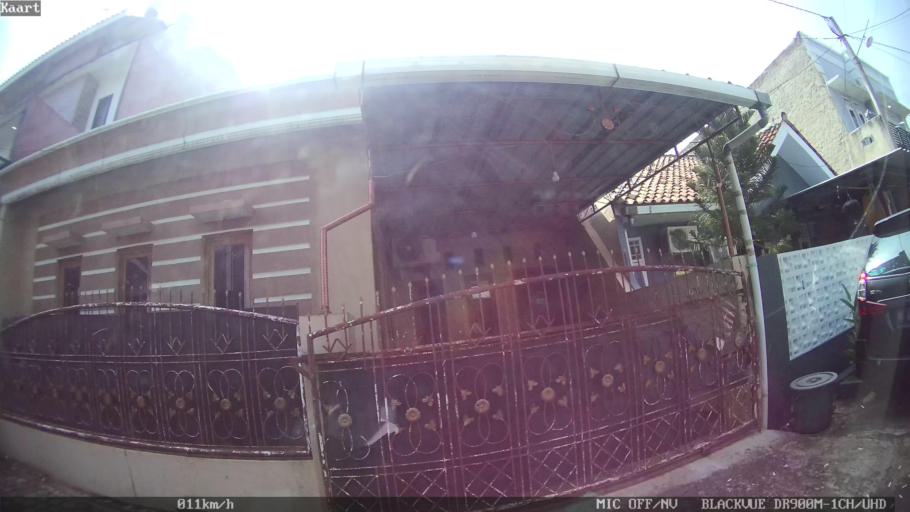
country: ID
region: Lampung
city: Kedaton
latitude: -5.4001
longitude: 105.2294
